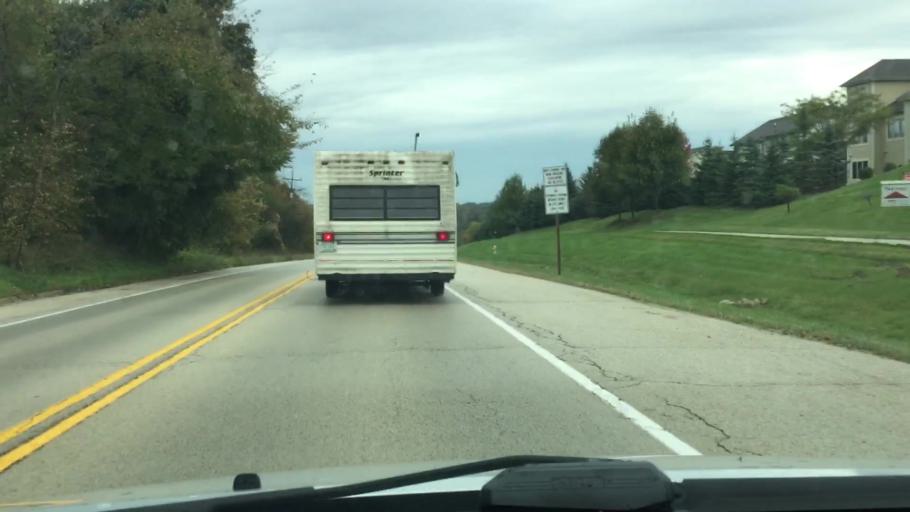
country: US
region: Wisconsin
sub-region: Waukesha County
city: Waukesha
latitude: 43.0218
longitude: -88.2997
